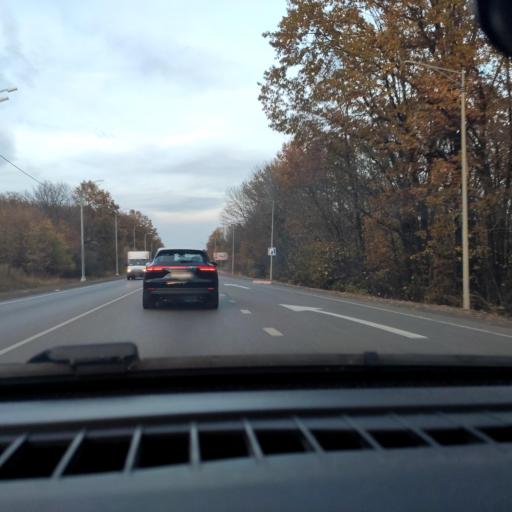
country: RU
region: Voronezj
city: Semiluki
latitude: 51.6465
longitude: 39.0246
